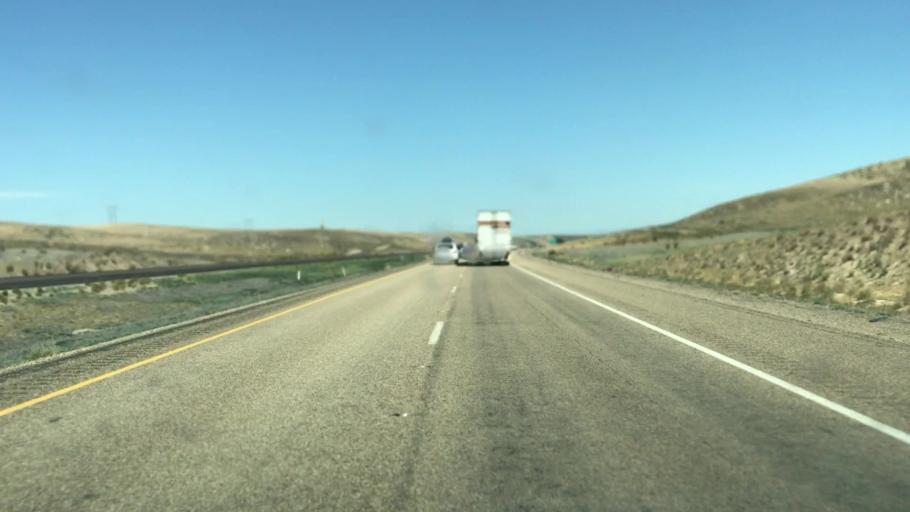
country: US
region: Idaho
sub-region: Payette County
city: New Plymouth
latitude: 43.8845
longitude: -116.8010
